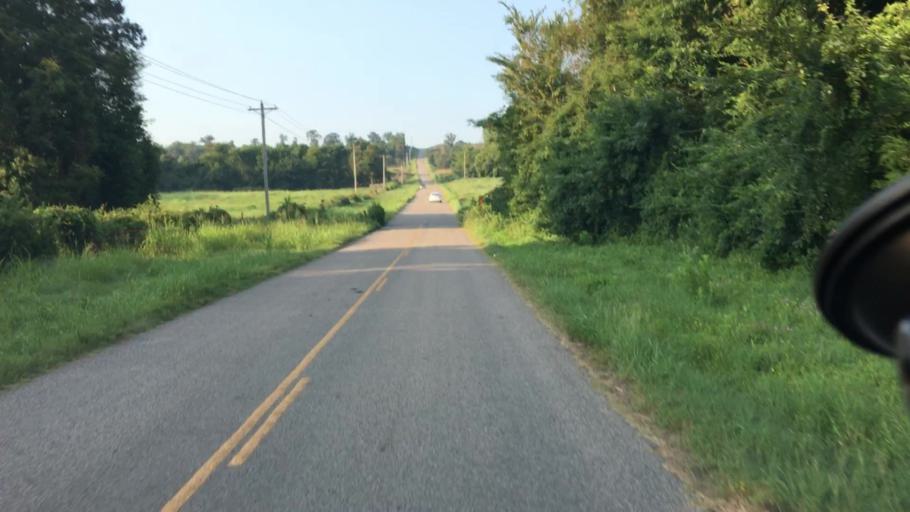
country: US
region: Arkansas
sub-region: Johnson County
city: Coal Hill
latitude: 35.3654
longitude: -93.6129
